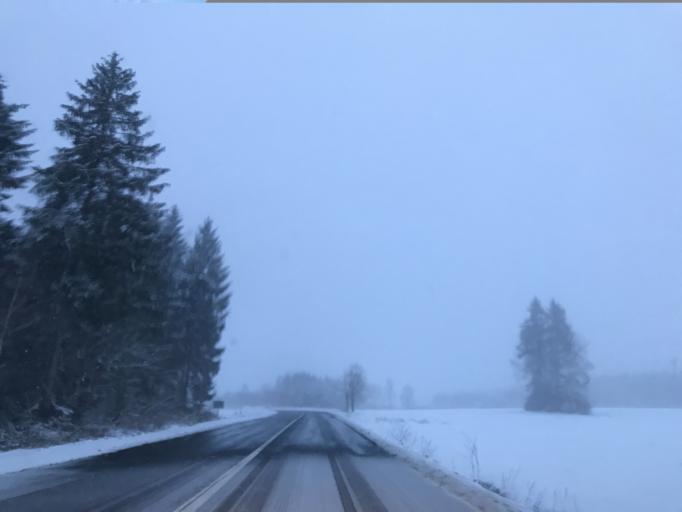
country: FR
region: Auvergne
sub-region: Departement du Puy-de-Dome
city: Saint-Sauves-d'Auvergne
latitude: 45.6526
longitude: 2.7007
